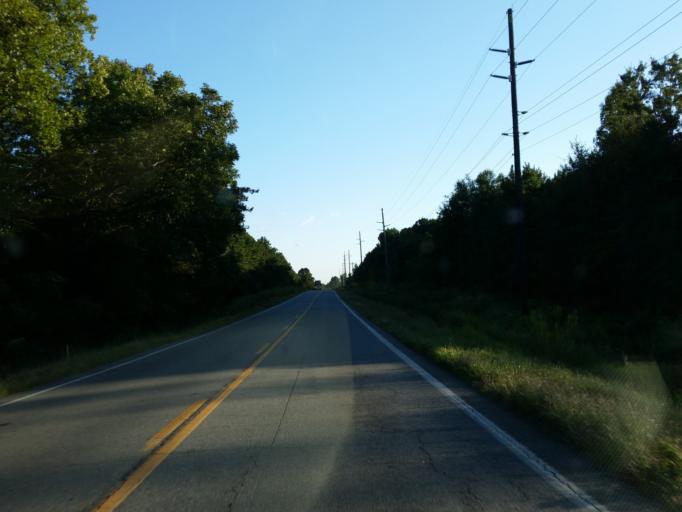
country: US
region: Georgia
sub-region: Dooly County
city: Vienna
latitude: 32.1037
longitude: -83.7784
